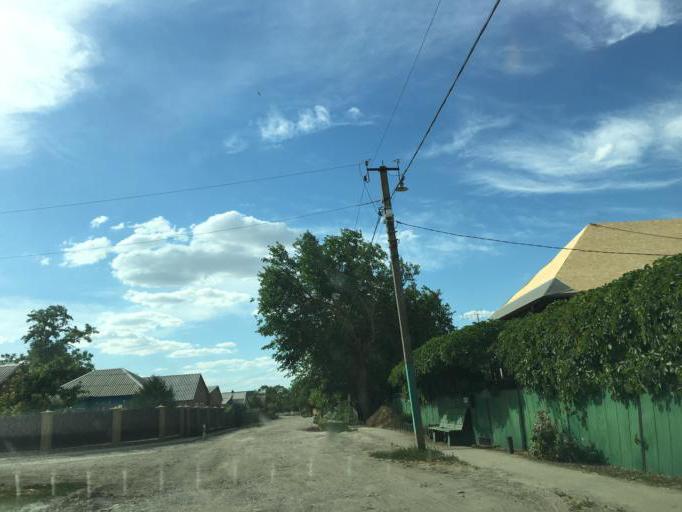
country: RU
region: Krasnodarskiy
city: Kushchevskaya
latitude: 46.5644
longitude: 39.6430
